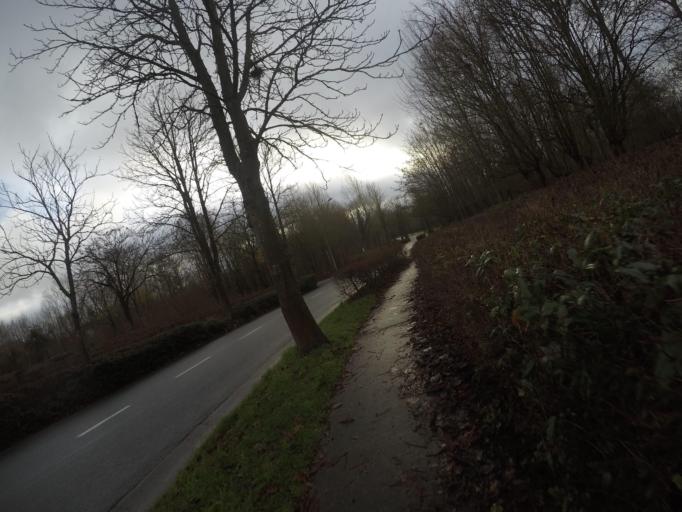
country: BE
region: Flanders
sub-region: Provincie Vlaams-Brabant
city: Liedekerke
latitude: 50.8641
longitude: 4.0795
